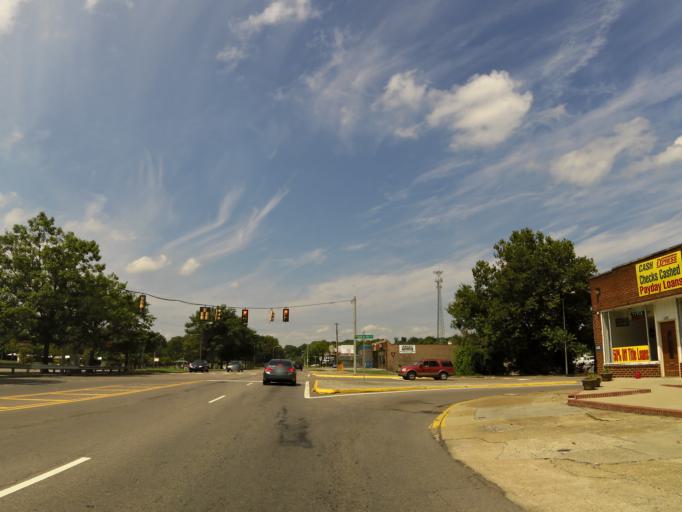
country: US
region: Tennessee
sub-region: Sullivan County
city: Kingsport
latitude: 36.5525
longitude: -82.5697
